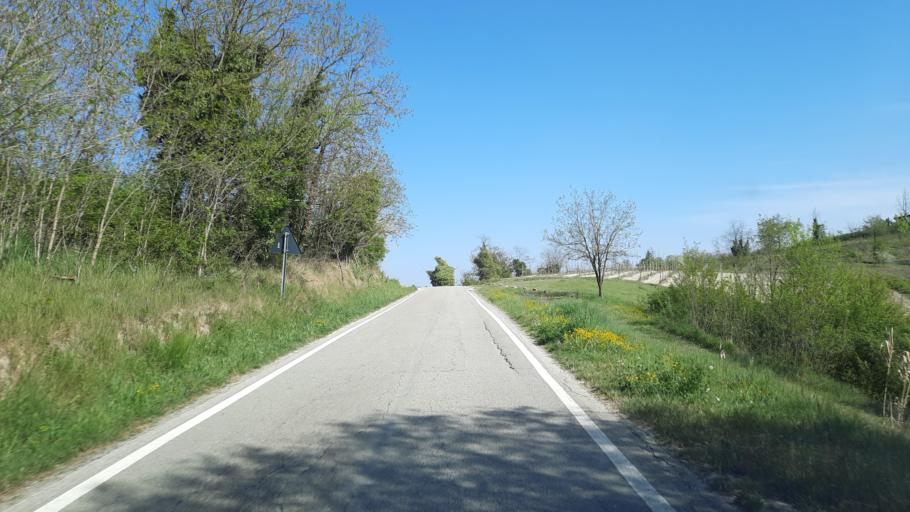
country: IT
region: Piedmont
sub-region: Provincia di Alessandria
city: Camagna Monferrato
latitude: 45.0130
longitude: 8.4204
